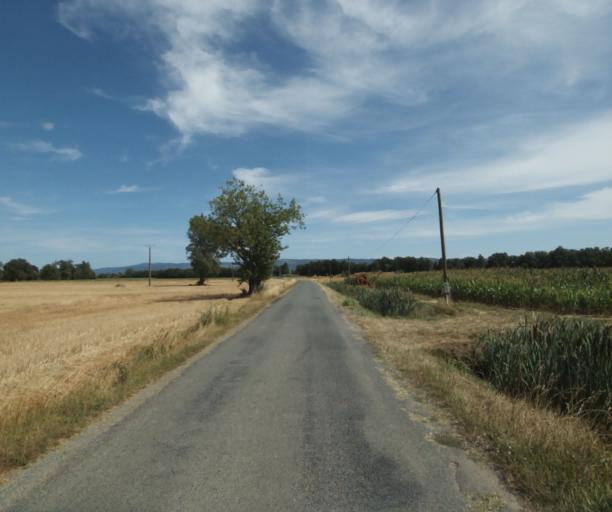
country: FR
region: Midi-Pyrenees
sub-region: Departement du Tarn
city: Puylaurens
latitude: 43.5176
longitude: 2.0172
